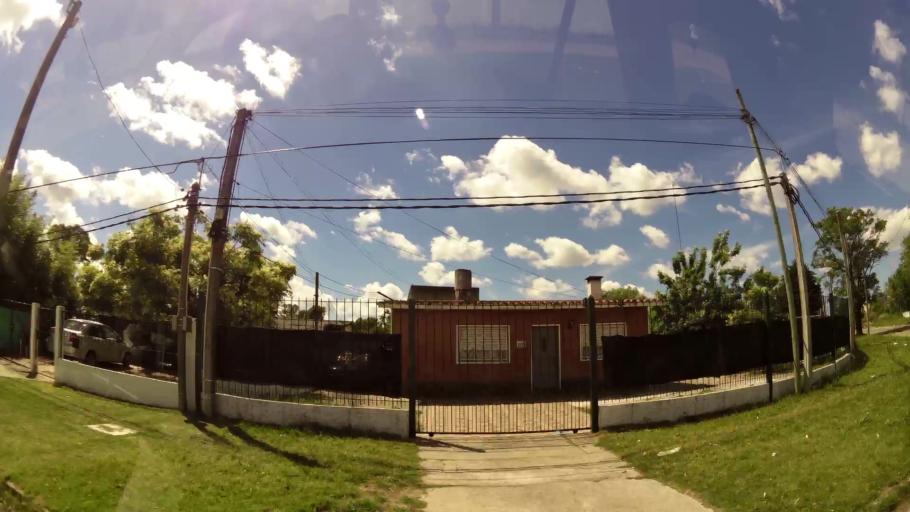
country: UY
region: Canelones
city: Paso de Carrasco
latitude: -34.8411
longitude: -56.1280
